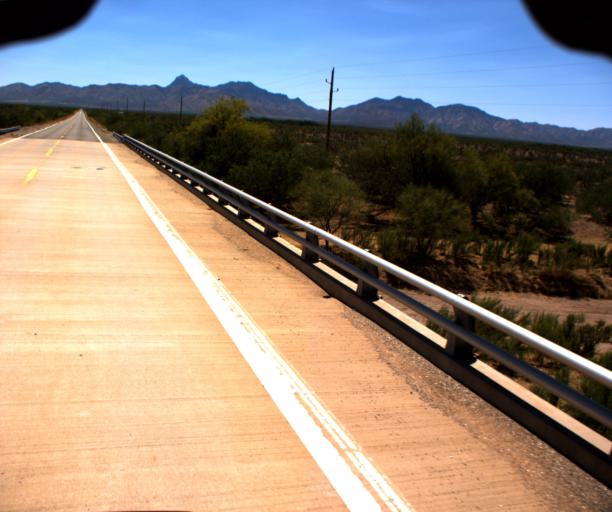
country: US
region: Arizona
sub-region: Pima County
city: Three Points
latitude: 31.8390
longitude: -111.4043
